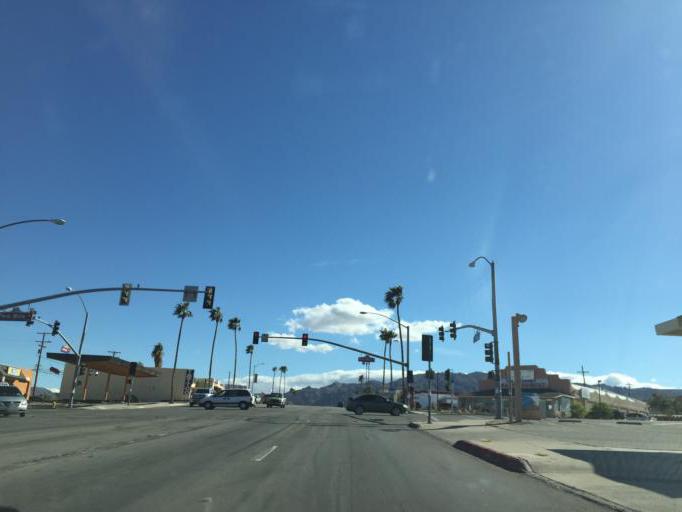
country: US
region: California
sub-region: San Bernardino County
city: Twentynine Palms
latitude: 34.1507
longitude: -116.0543
